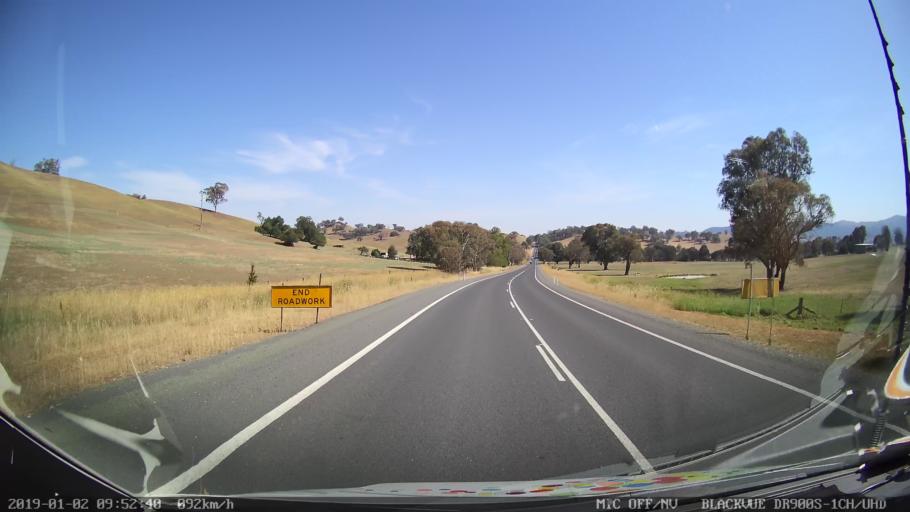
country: AU
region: New South Wales
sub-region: Tumut Shire
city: Tumut
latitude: -35.2581
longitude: 148.2045
